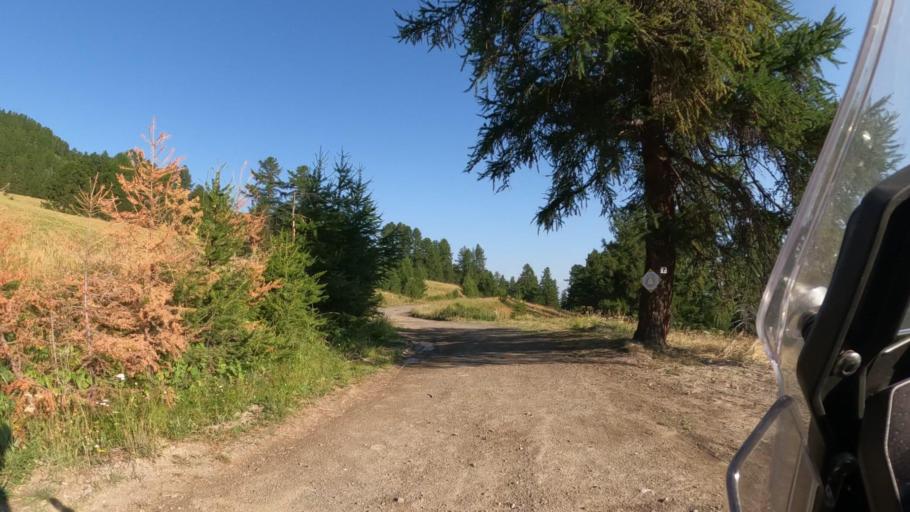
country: FR
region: Provence-Alpes-Cote d'Azur
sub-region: Departement des Hautes-Alpes
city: Guillestre
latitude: 44.6106
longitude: 6.6671
